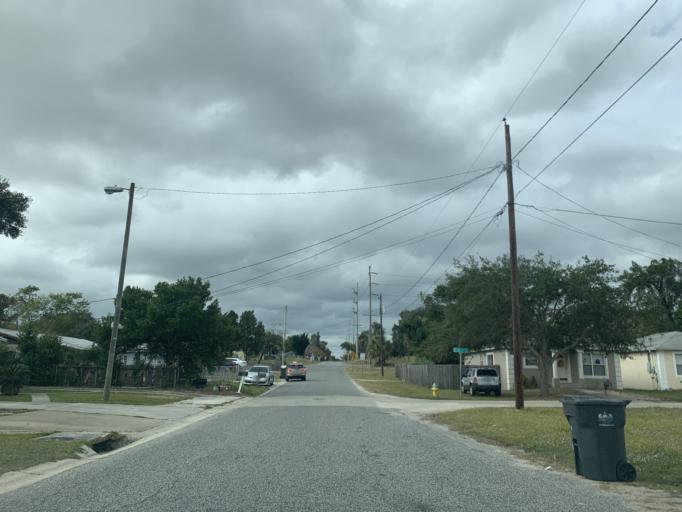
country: US
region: Florida
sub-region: Hillsborough County
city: East Lake-Orient Park
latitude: 27.9778
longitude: -82.3926
